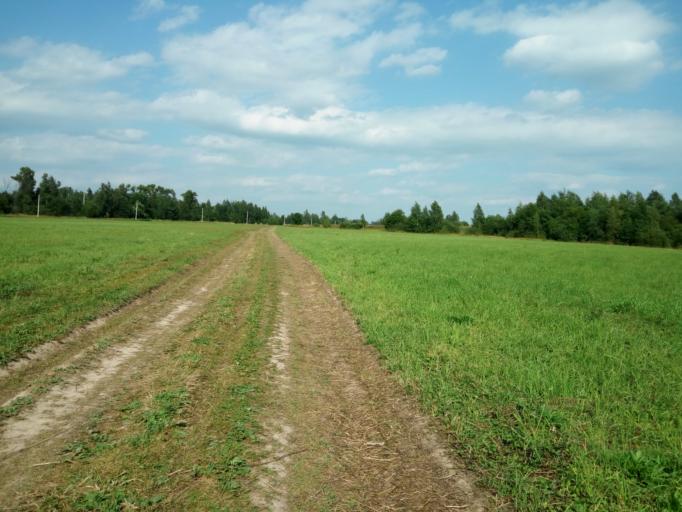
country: RU
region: Moskovskaya
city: Kubinka
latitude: 55.5853
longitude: 36.7382
